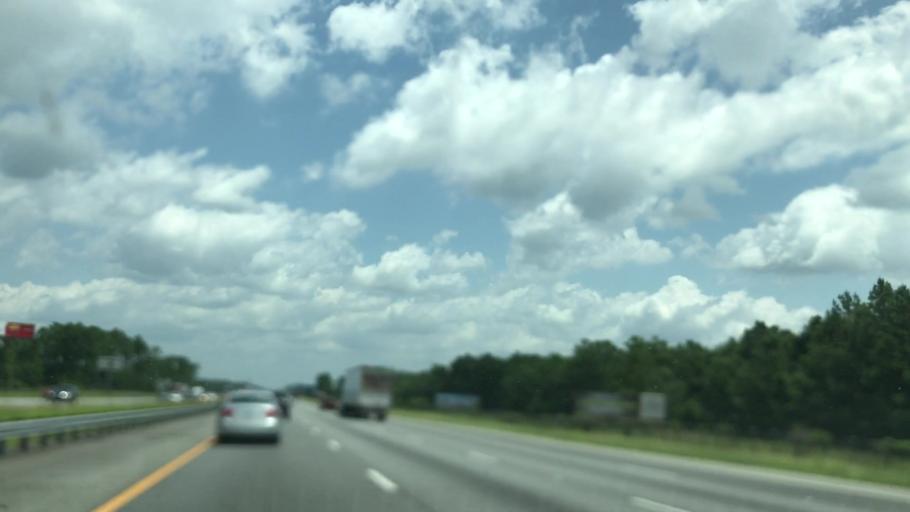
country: US
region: Georgia
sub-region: Glynn County
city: Brunswick
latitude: 31.1103
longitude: -81.5915
